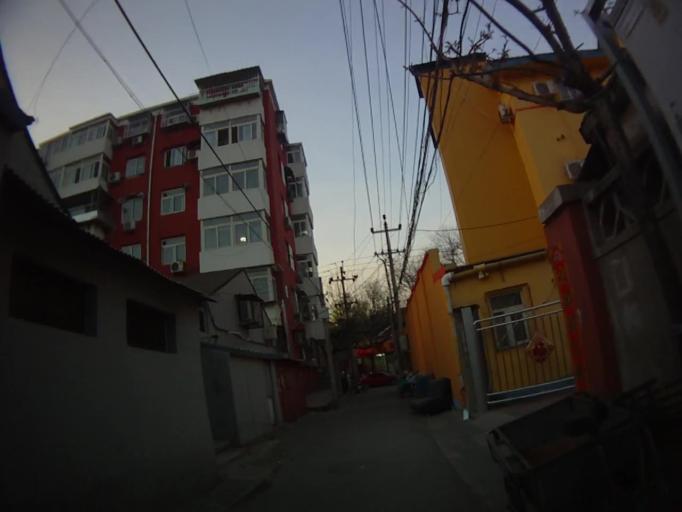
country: CN
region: Beijing
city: Longtan
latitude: 39.8844
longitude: 116.4270
